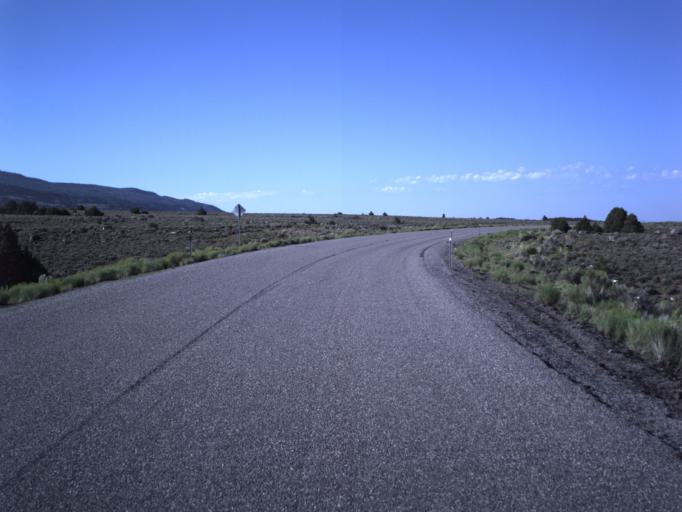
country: US
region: Utah
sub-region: Wayne County
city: Loa
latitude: 38.5059
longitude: -111.5300
